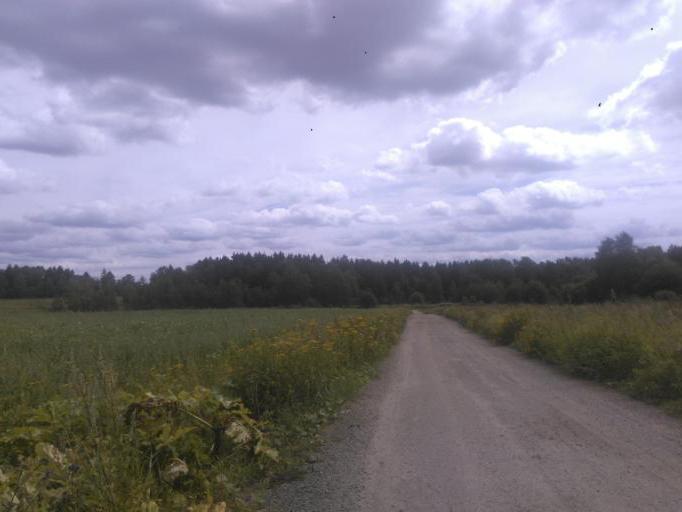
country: RU
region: Moskovskaya
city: Solnechnogorsk
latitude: 56.1415
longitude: 36.9270
